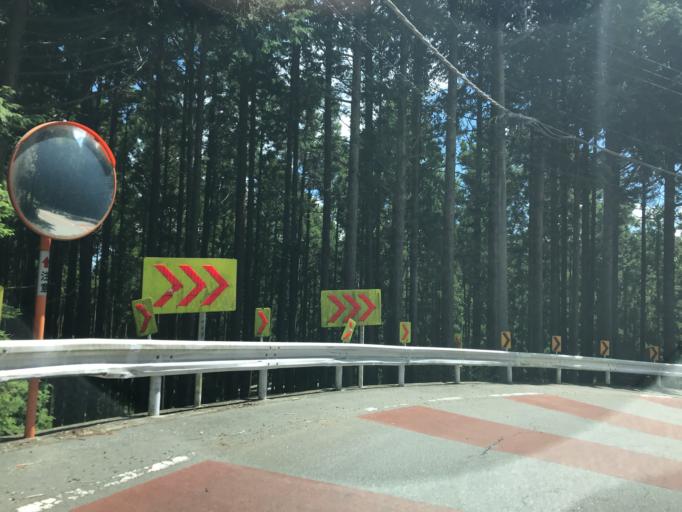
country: JP
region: Shizuoka
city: Gotemba
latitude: 35.2530
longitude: 138.8335
